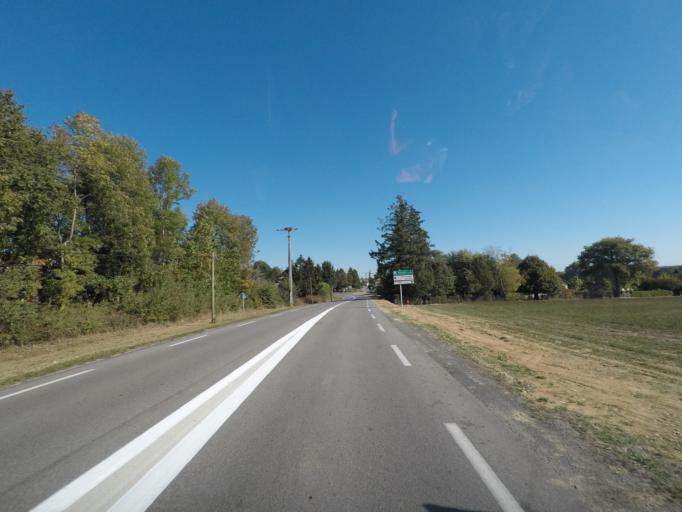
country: FR
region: Rhone-Alpes
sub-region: Departement de l'Ain
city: Saint-Paul-de-Varax
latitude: 46.0946
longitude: 5.1227
